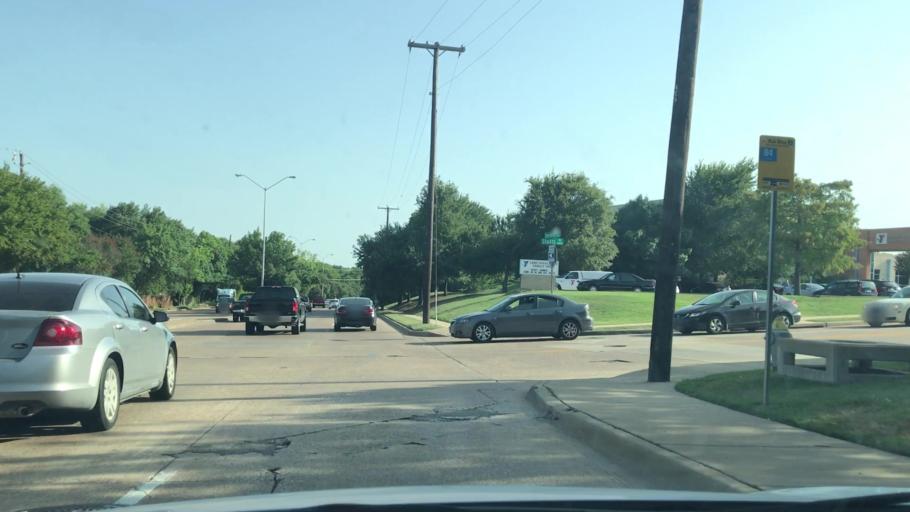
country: US
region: Texas
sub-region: Dallas County
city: Richardson
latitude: 32.9049
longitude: -96.7486
